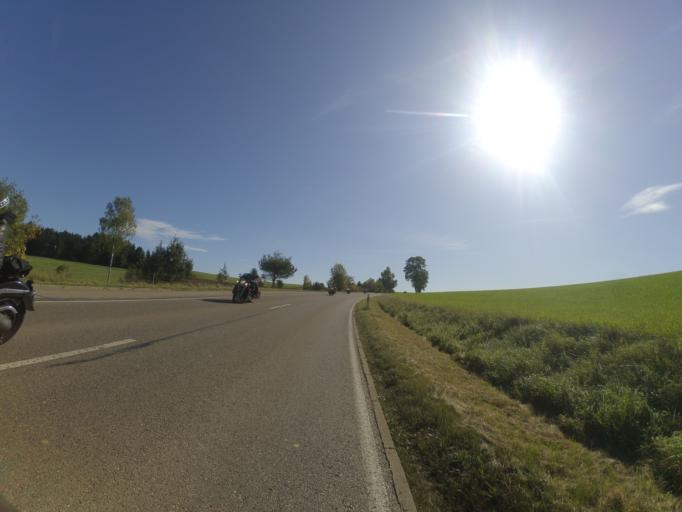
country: DE
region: Baden-Wuerttemberg
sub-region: Tuebingen Region
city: Borslingen
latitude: 48.5456
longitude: 10.0515
